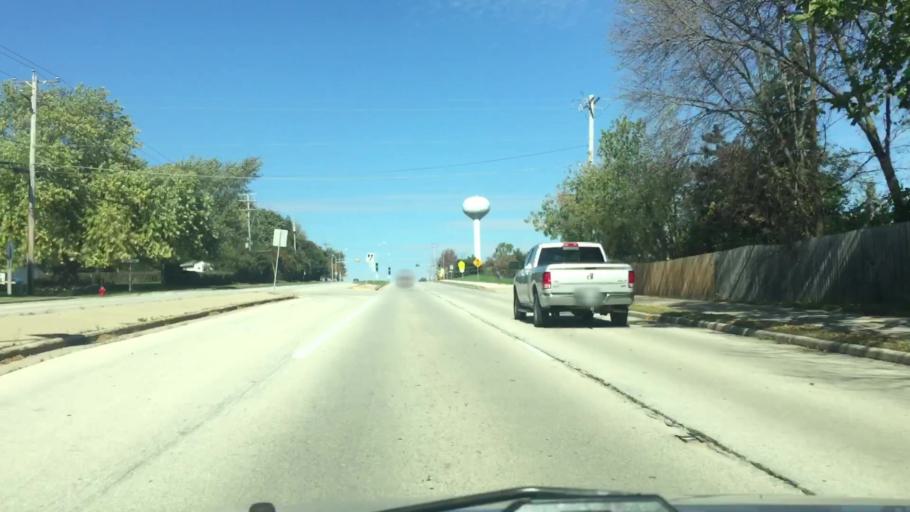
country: US
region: Wisconsin
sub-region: Waukesha County
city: Waukesha
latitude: 43.0281
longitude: -88.1668
